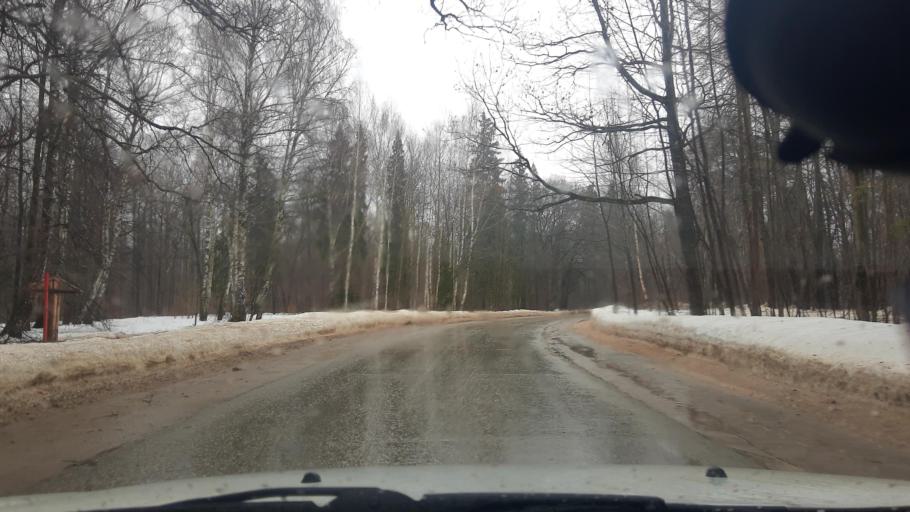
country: RU
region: Nizjnij Novgorod
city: Afonino
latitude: 56.1798
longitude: 44.0118
